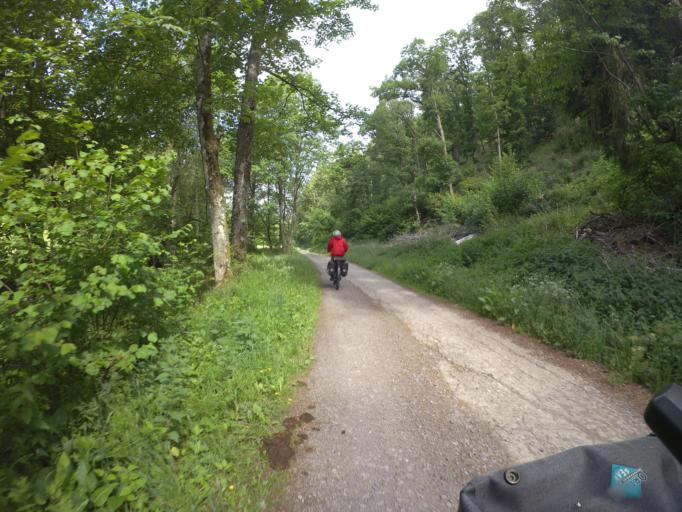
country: DE
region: North Rhine-Westphalia
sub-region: Regierungsbezirk Koln
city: Hellenthal
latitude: 50.4600
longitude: 6.4245
